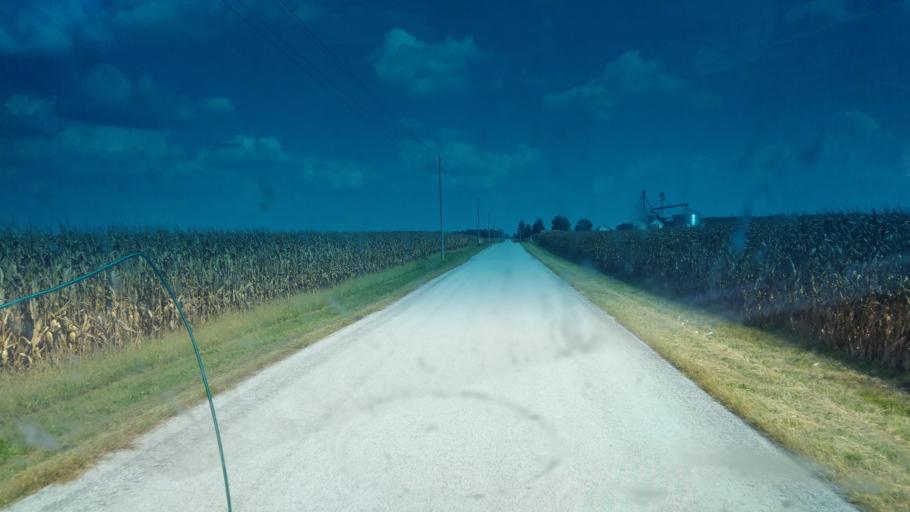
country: US
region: Ohio
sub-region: Hardin County
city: Kenton
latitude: 40.6593
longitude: -83.7166
